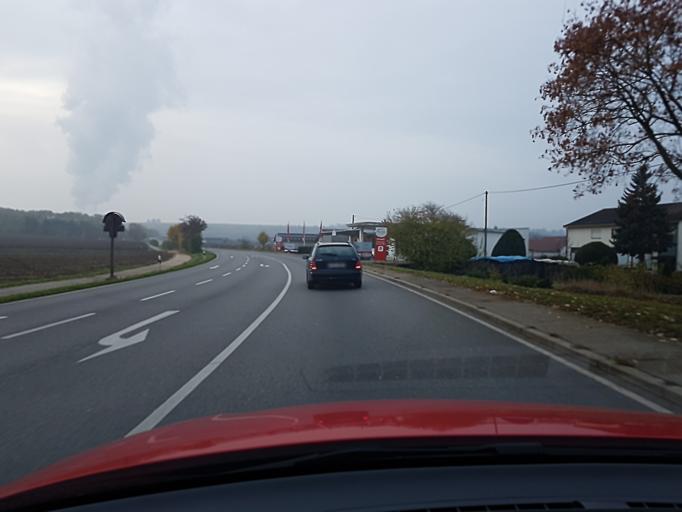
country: DE
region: Baden-Wuerttemberg
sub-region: Regierungsbezirk Stuttgart
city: Lauffen am Neckar
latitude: 49.0696
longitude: 9.1573
